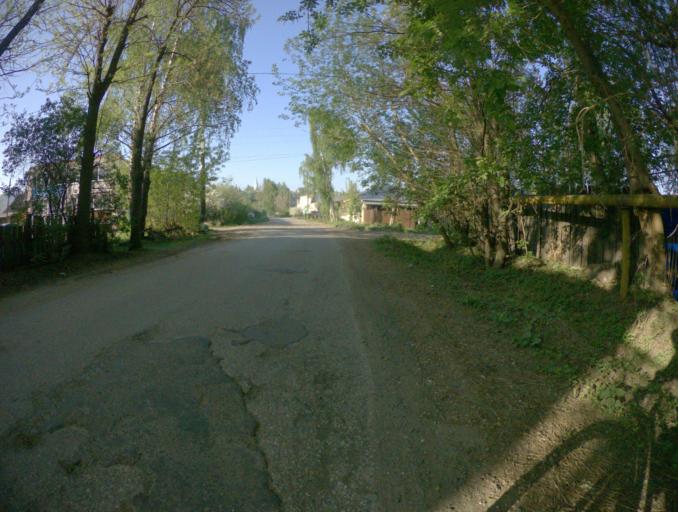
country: RU
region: Vladimir
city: Vyazniki
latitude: 56.2485
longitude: 42.1676
